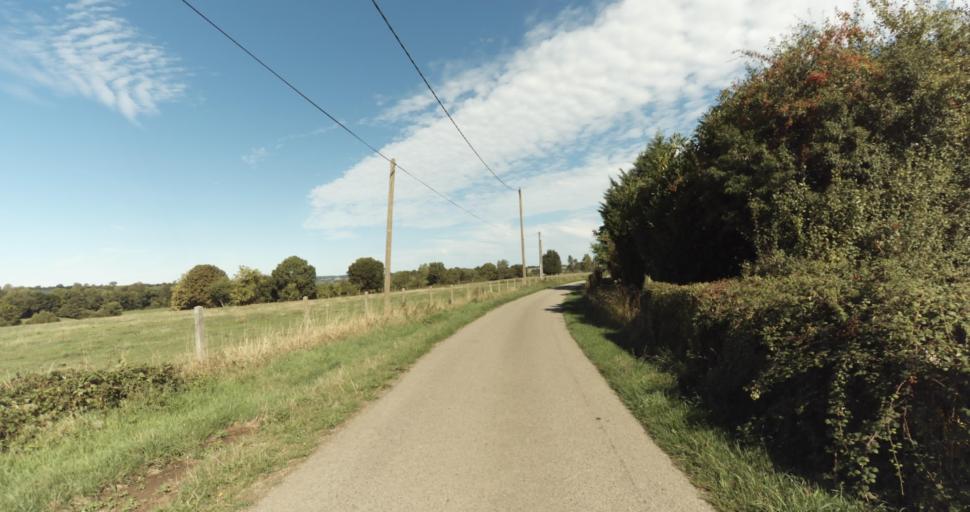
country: FR
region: Lower Normandy
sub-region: Departement de l'Orne
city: Gace
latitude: 48.7979
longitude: 0.2320
